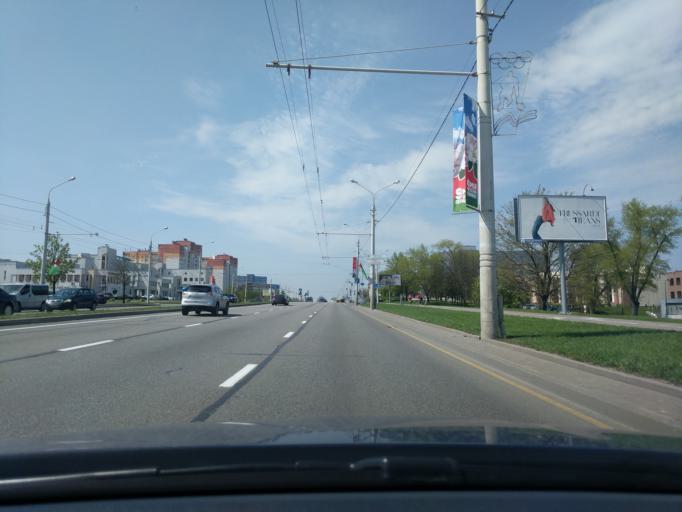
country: BY
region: Minsk
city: Minsk
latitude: 53.9331
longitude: 27.5052
